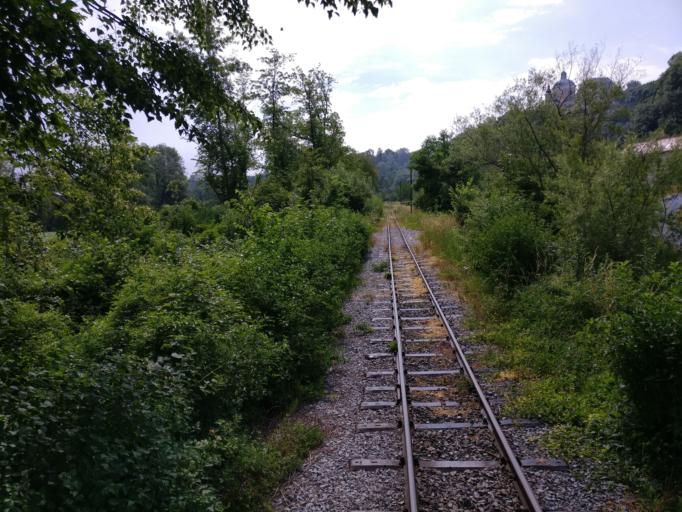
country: AT
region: Upper Austria
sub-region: Politischer Bezirk Steyr-Land
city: Garsten
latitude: 48.0409
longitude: 14.3843
